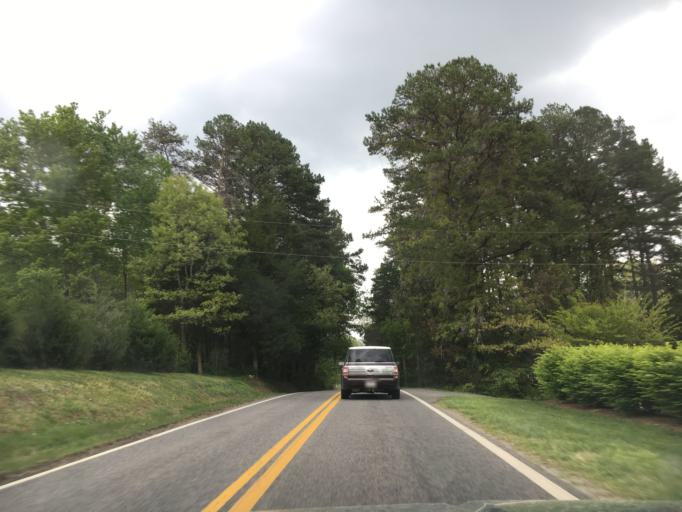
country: US
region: Virginia
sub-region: Campbell County
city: Rustburg
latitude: 37.3319
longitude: -79.1104
